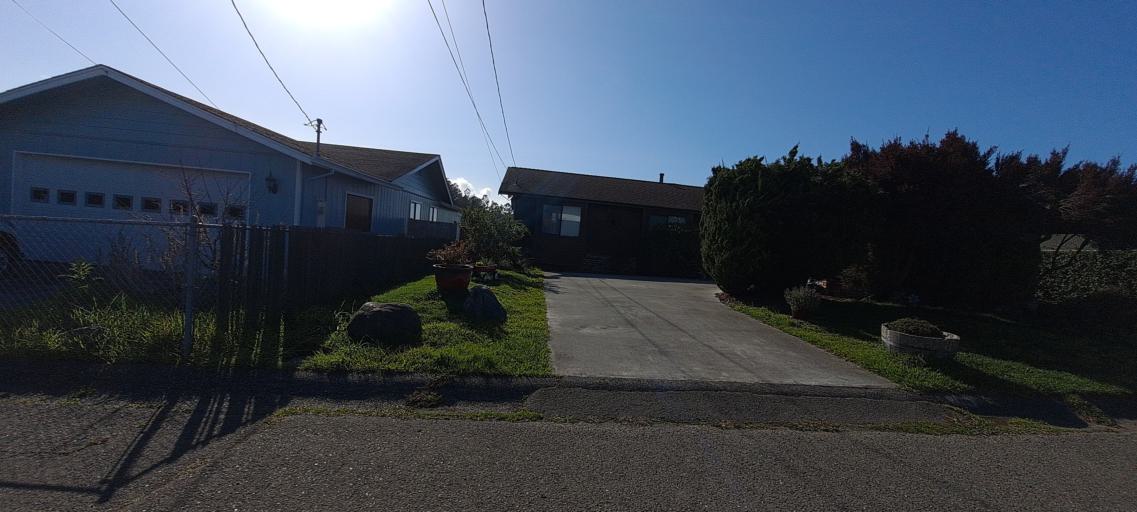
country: US
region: California
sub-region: Humboldt County
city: Fortuna
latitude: 40.5765
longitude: -124.1403
